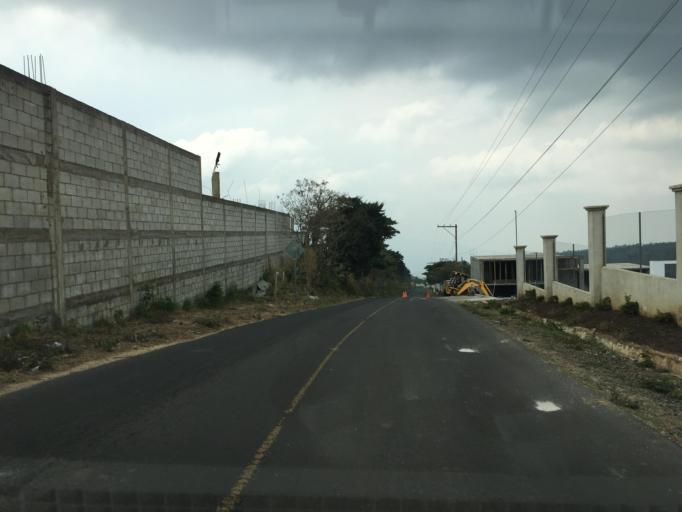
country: GT
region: Escuintla
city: San Vicente Pacaya
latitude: 14.3360
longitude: -90.5656
